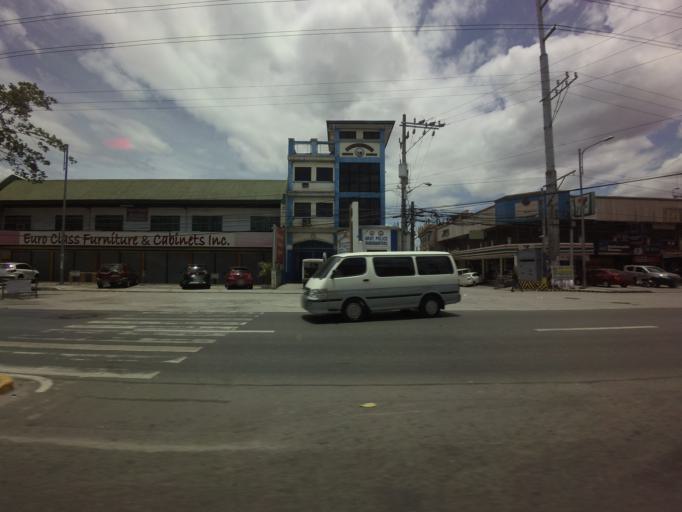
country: PH
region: Metro Manila
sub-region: Marikina
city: Calumpang
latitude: 14.6105
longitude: 121.1035
